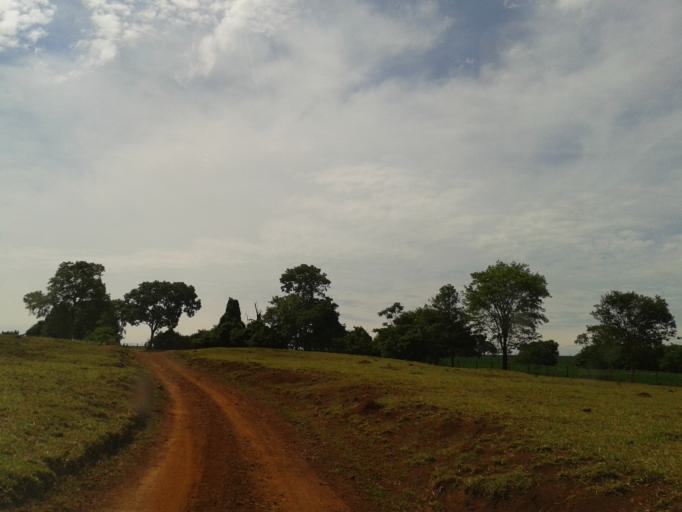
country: BR
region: Minas Gerais
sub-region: Centralina
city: Centralina
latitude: -18.7028
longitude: -49.2057
